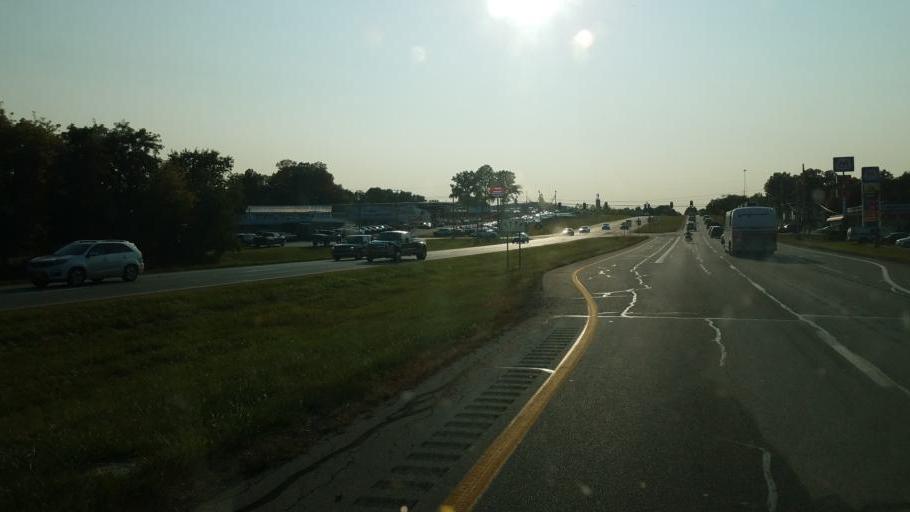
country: US
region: Ohio
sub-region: Wayne County
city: Dalton
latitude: 40.7951
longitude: -81.6925
